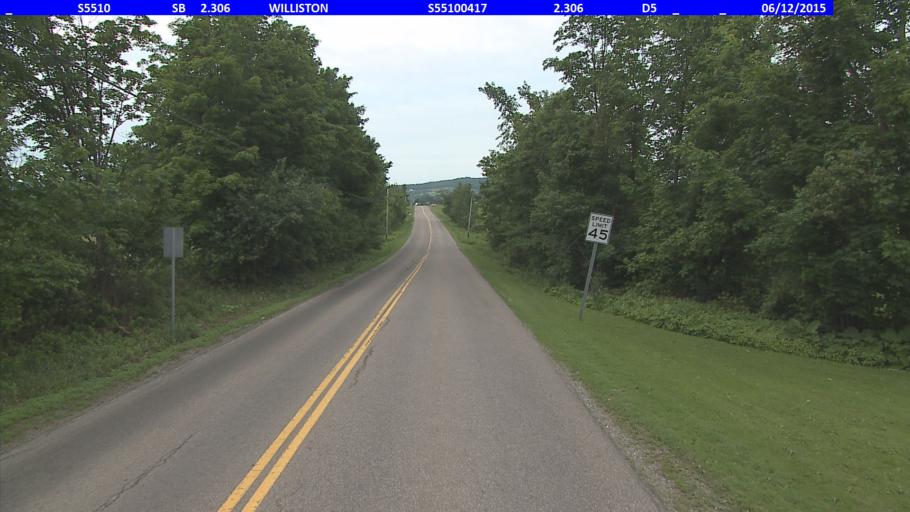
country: US
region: Vermont
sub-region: Chittenden County
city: Williston
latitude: 44.4050
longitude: -73.0902
